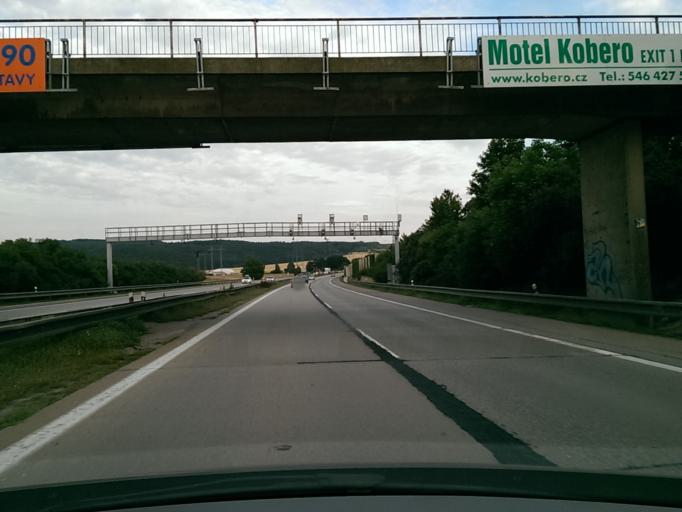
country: CZ
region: South Moravian
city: Ricany
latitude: 49.2197
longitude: 16.4029
